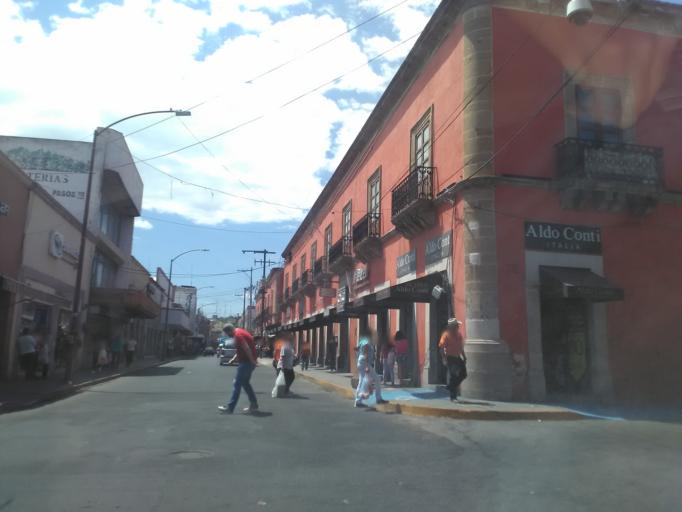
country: MX
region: Durango
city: Victoria de Durango
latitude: 24.0240
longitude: -104.6662
